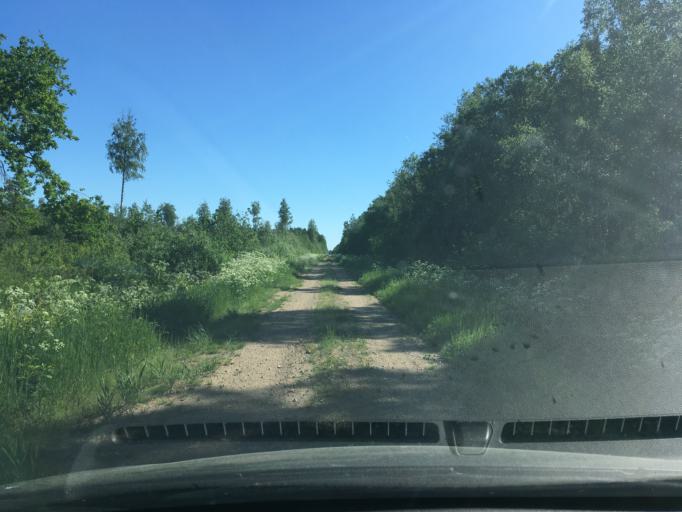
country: EE
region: Laeaene
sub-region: Lihula vald
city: Lihula
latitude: 58.6338
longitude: 23.7487
